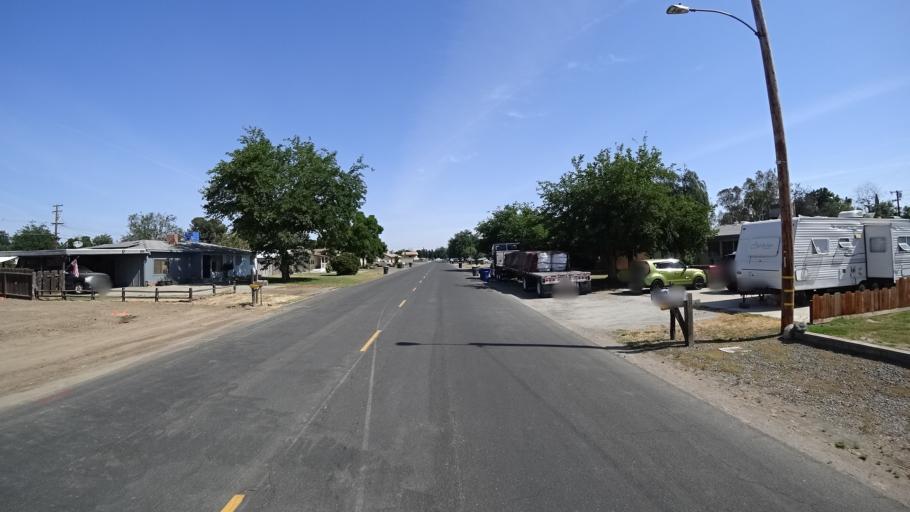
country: US
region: California
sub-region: Kings County
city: Hanford
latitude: 36.3400
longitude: -119.6714
